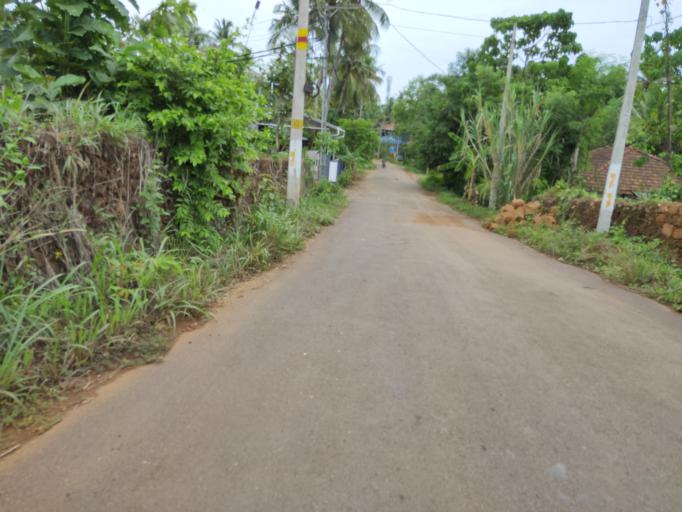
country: IN
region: Kerala
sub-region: Malappuram
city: Manjeri
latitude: 11.2478
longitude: 76.2481
